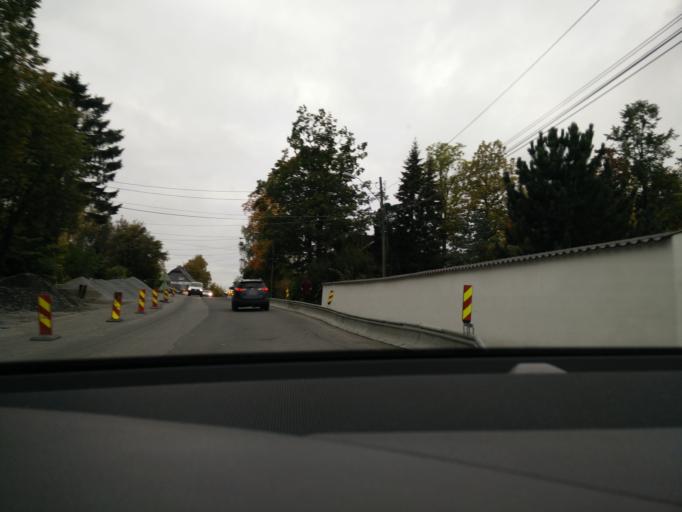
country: NO
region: Akershus
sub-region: Baerum
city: Lysaker
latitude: 59.9306
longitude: 10.6174
